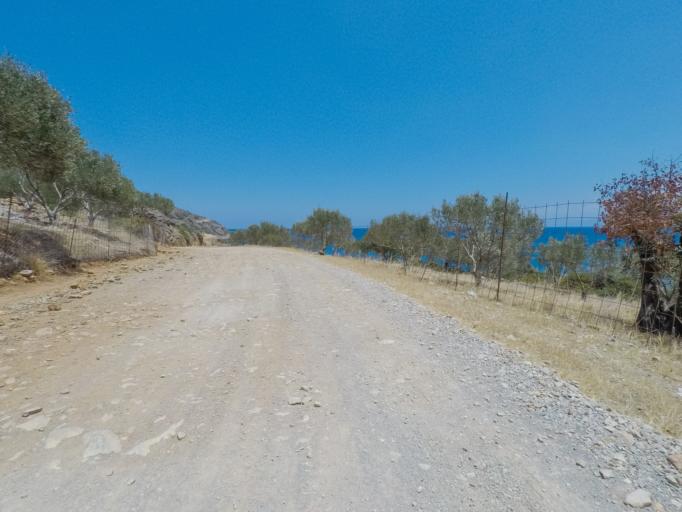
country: GR
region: Crete
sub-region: Nomos Lasithiou
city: Elounda
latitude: 35.3055
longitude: 25.7322
